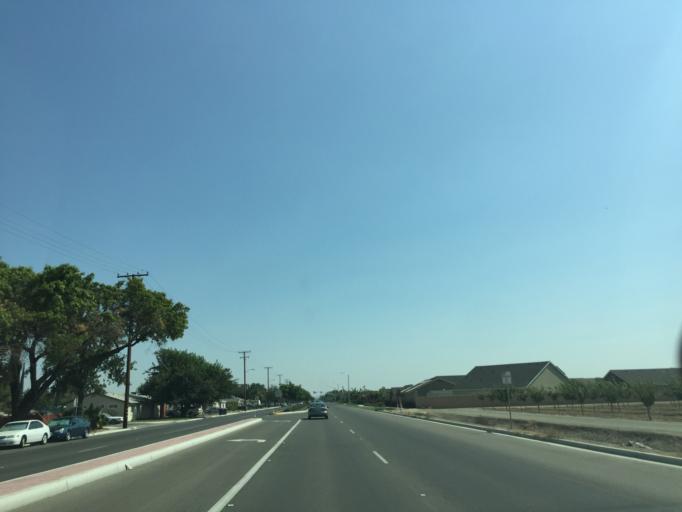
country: US
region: California
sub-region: Kings County
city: Hanford
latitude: 36.3400
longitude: -119.6729
